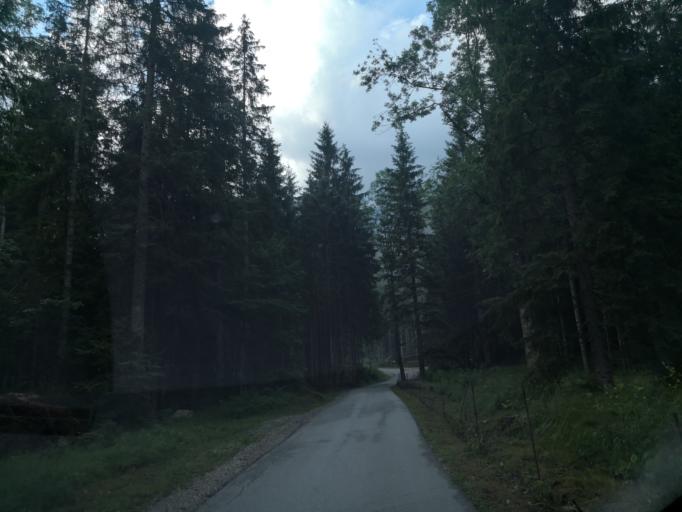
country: SI
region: Jezersko
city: Zgornje Jezersko
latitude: 46.3977
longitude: 14.5265
